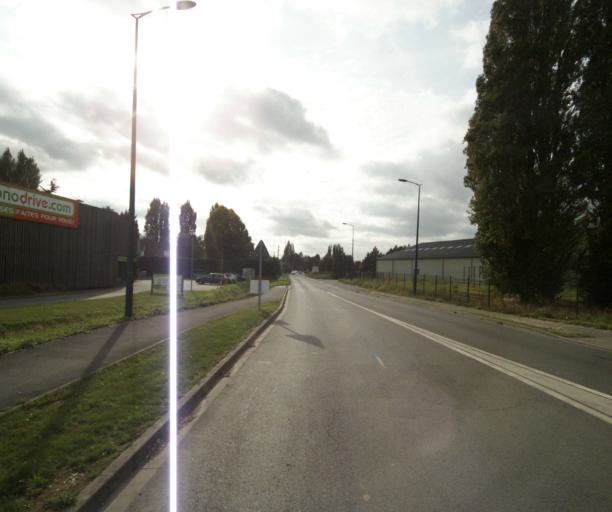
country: FR
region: Nord-Pas-de-Calais
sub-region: Departement du Nord
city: Bois-Grenier
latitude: 50.6581
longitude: 2.8911
